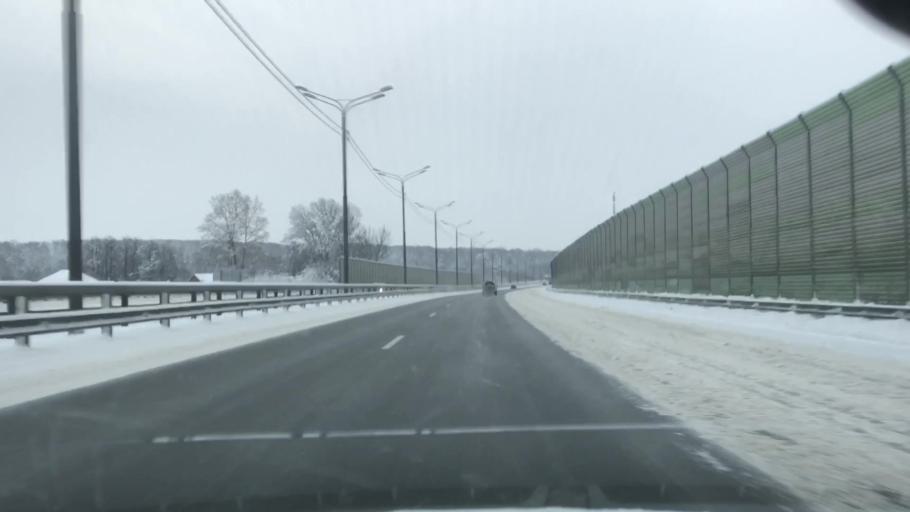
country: RU
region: Moskovskaya
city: Barybino
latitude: 55.2808
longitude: 37.8626
